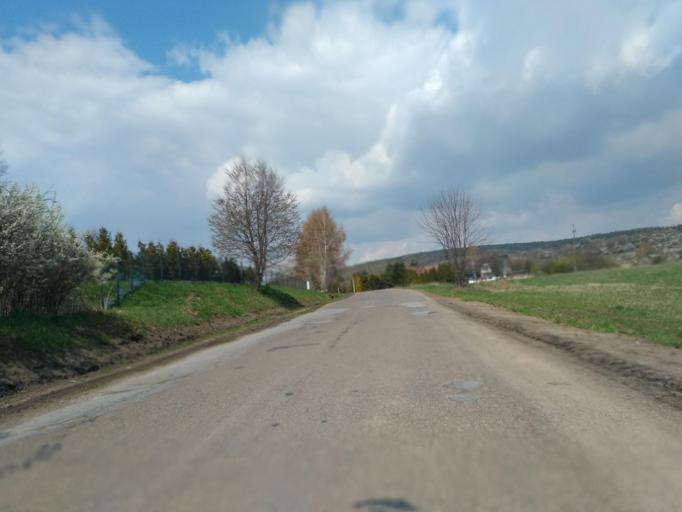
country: PL
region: Subcarpathian Voivodeship
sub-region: Powiat sanocki
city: Nowosielce-Gniewosz
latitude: 49.5540
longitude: 22.1063
